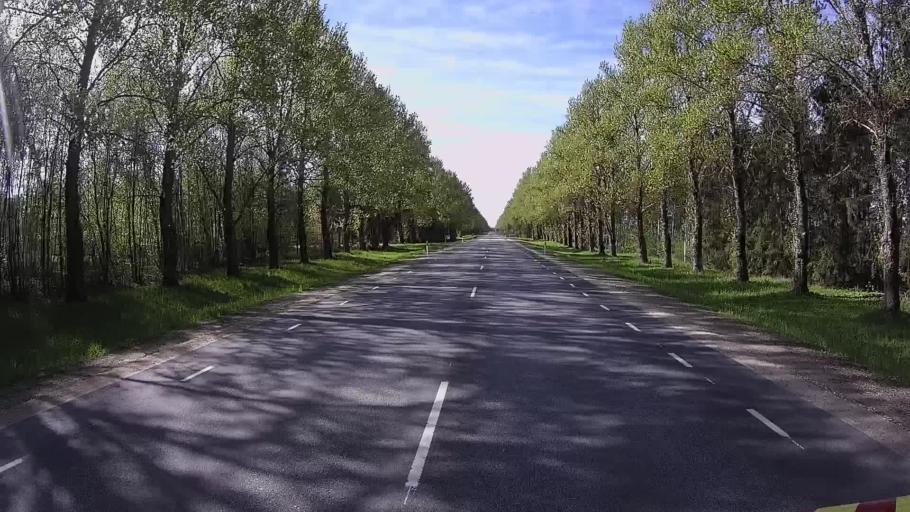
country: EE
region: Polvamaa
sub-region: Polva linn
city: Polva
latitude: 58.2968
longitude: 27.0014
